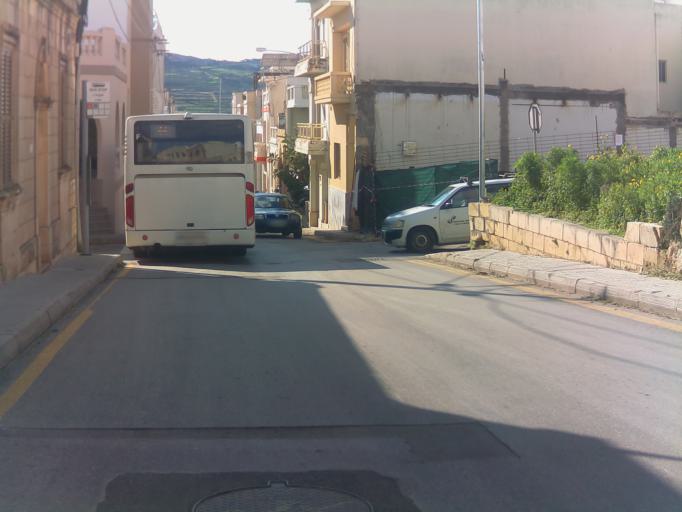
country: MT
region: L-Imgarr
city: Imgarr
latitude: 35.9219
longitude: 14.3669
